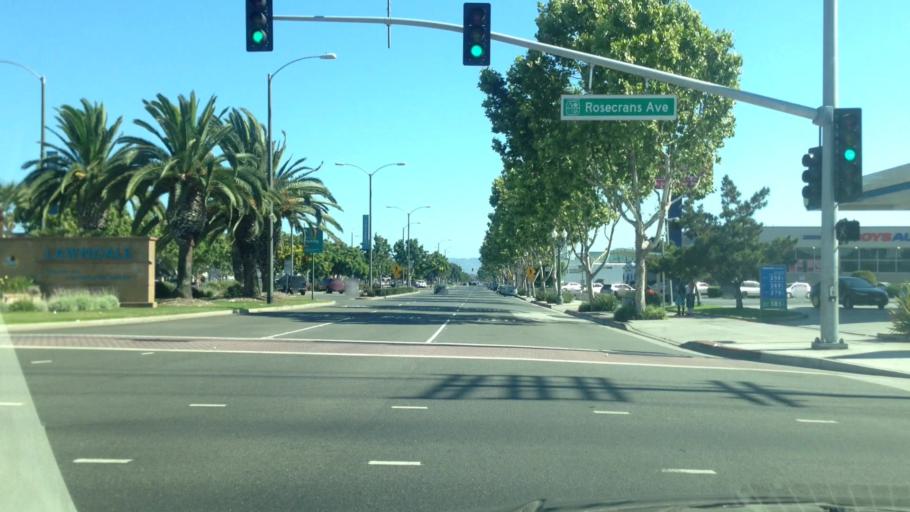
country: US
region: California
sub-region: Los Angeles County
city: Hawthorne
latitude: 33.9020
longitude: -118.3528
